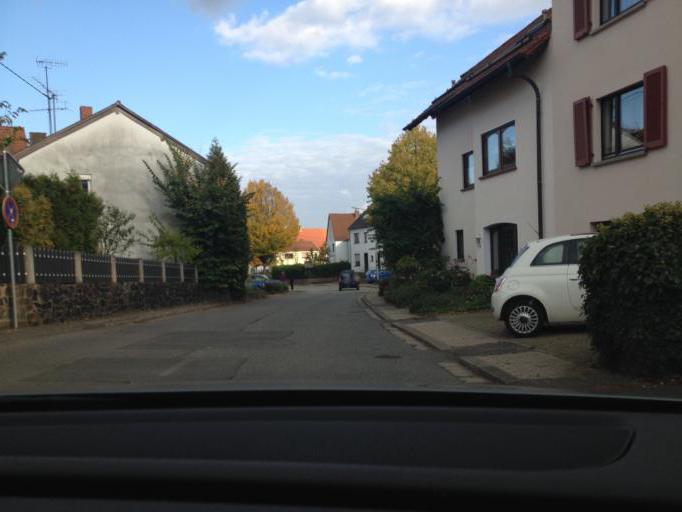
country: DE
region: Rheinland-Pfalz
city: Reichweiler
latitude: 49.5245
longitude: 7.2583
